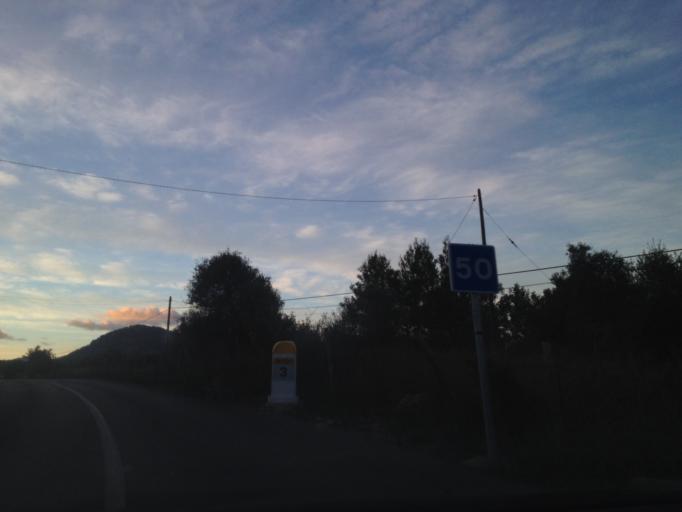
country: ES
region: Balearic Islands
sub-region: Illes Balears
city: Pollenca
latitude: 39.8568
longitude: 3.0547
